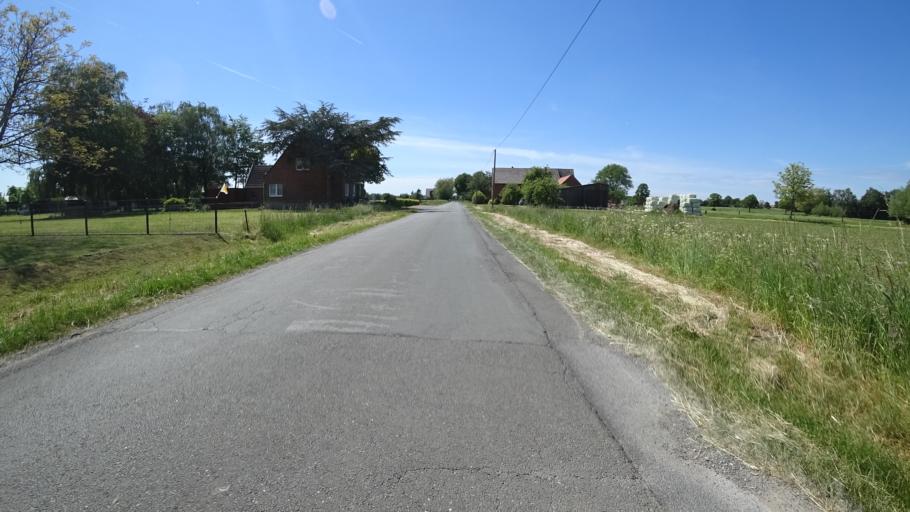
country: DE
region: North Rhine-Westphalia
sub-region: Regierungsbezirk Detmold
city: Rheda-Wiedenbruck
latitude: 51.8202
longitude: 8.2999
